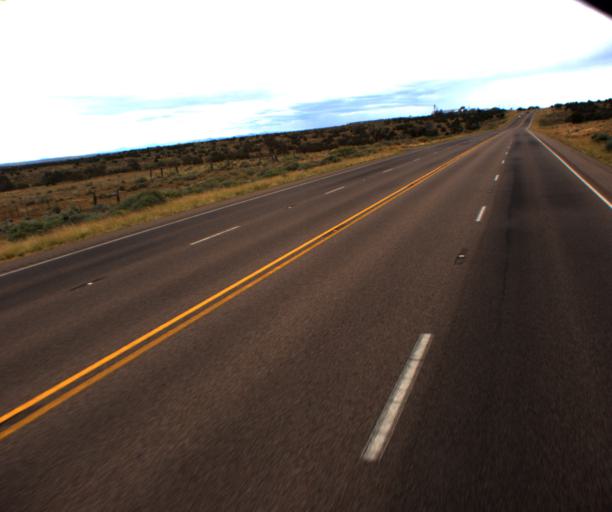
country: US
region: Arizona
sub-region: Navajo County
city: Snowflake
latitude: 34.5768
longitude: -110.0837
